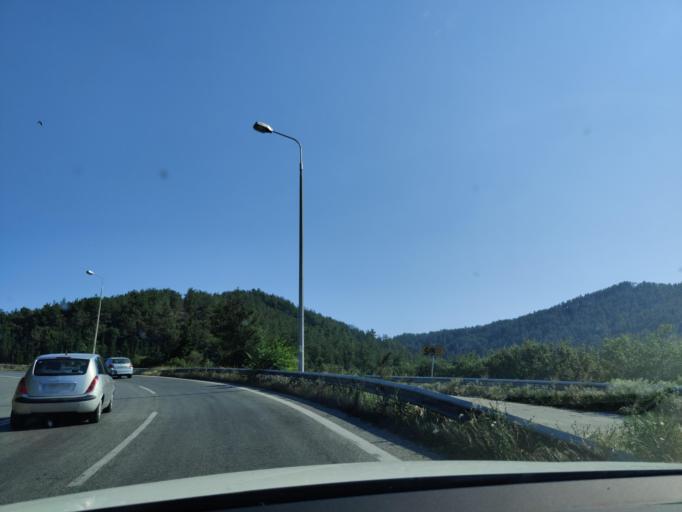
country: GR
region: East Macedonia and Thrace
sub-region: Nomos Kavalas
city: Amygdaleonas
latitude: 40.9472
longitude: 24.3714
